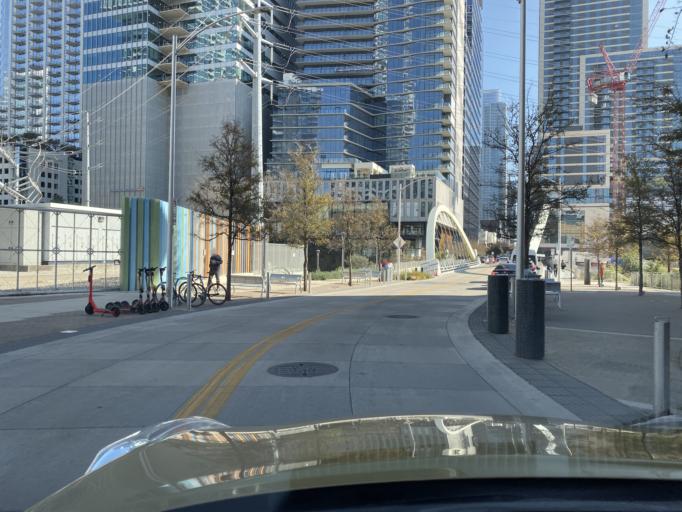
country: US
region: Texas
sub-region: Travis County
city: Austin
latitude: 30.2661
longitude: -97.7515
